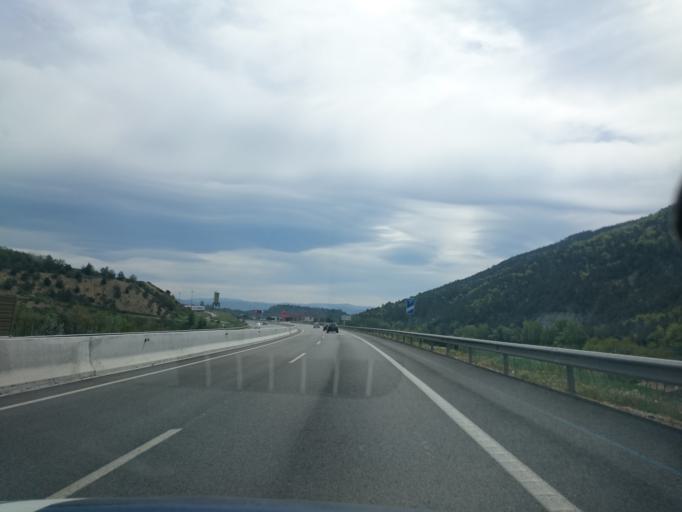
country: ES
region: Catalonia
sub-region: Provincia de Barcelona
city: Muntanyola
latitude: 41.9341
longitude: 2.1882
